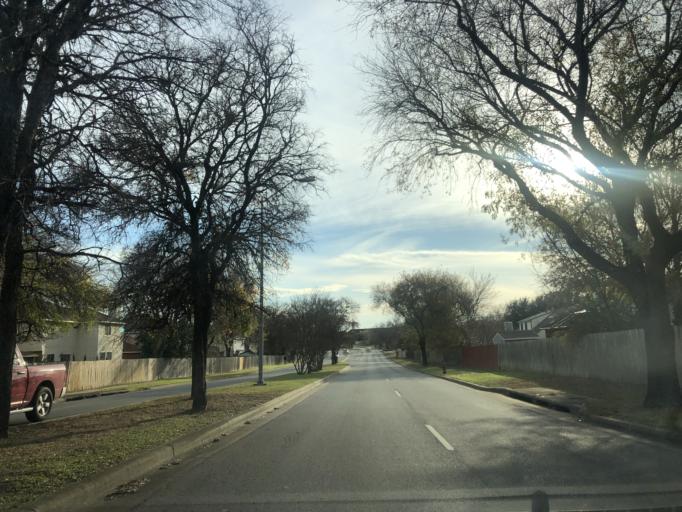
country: US
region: Texas
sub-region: Travis County
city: Windemere
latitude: 30.4577
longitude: -97.6346
